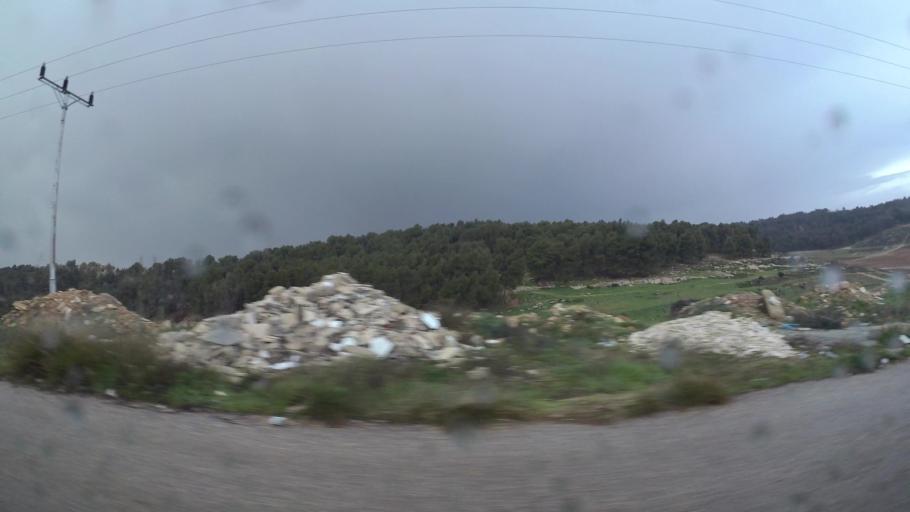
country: JO
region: Amman
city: Umm as Summaq
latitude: 31.8607
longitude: 35.8758
